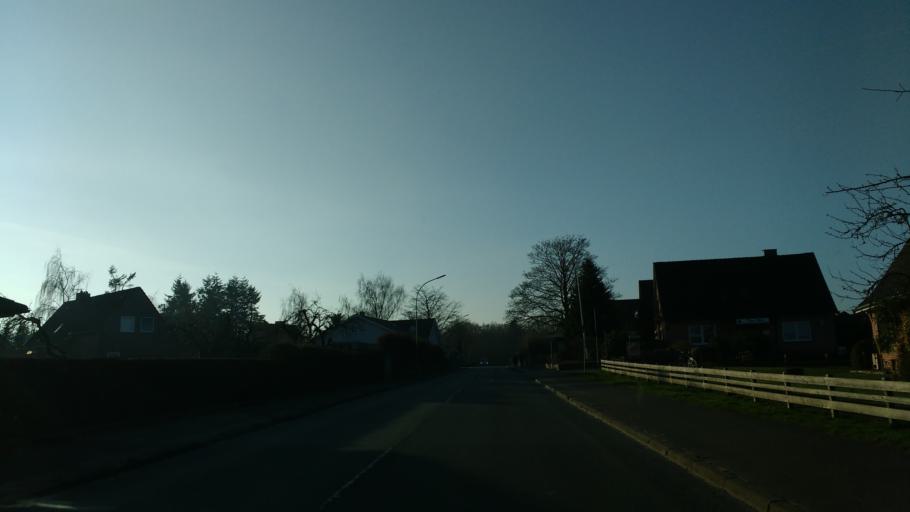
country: DE
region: Schleswig-Holstein
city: Hohenwestedt
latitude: 54.0951
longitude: 9.6678
